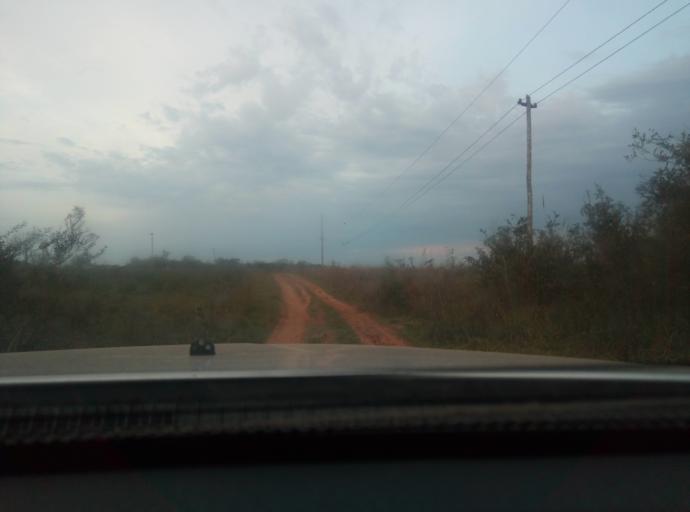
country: PY
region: Caaguazu
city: Carayao
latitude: -25.1486
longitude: -56.3859
